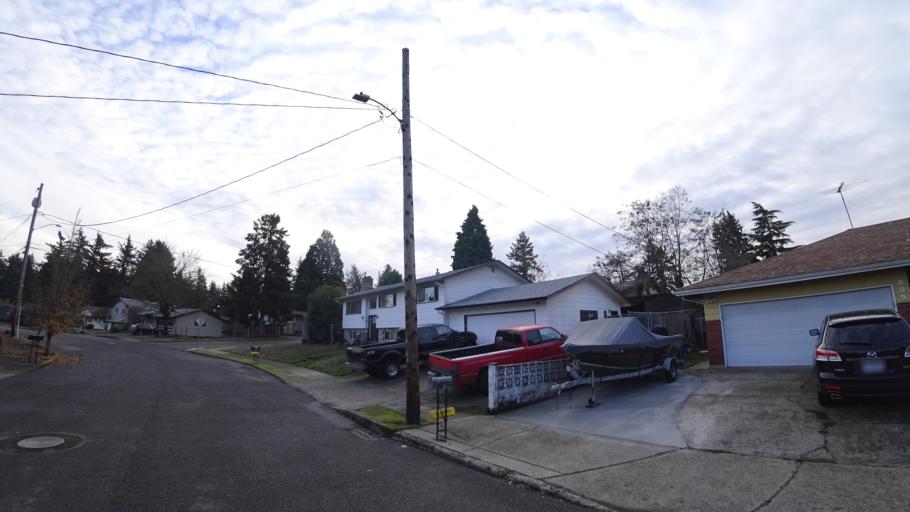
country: US
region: Oregon
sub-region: Multnomah County
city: Lents
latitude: 45.5168
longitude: -122.5239
